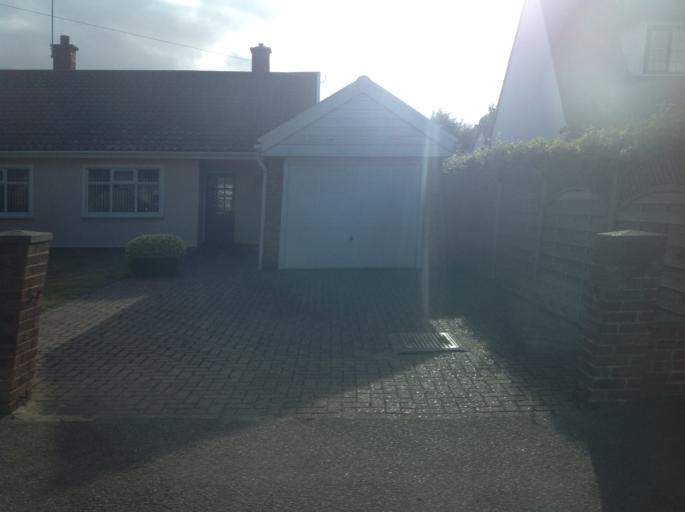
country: GB
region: England
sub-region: Suffolk
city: Felixstowe
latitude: 51.9696
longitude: 1.3522
